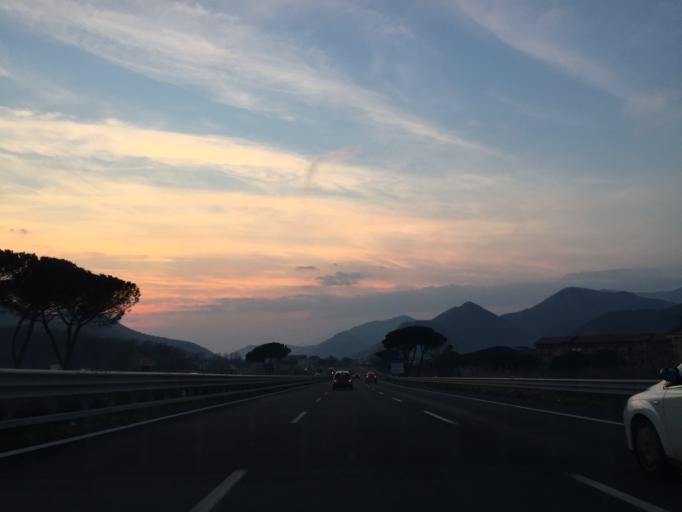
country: IT
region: Campania
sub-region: Provincia di Salerno
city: Faraldo-Nocelleto
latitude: 40.7733
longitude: 14.7687
